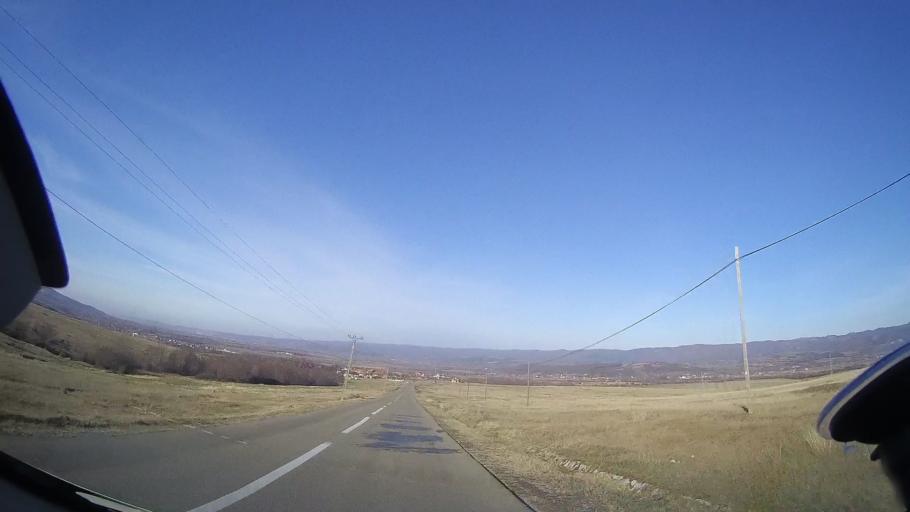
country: RO
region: Bihor
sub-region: Comuna Vadu Crisului
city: Vadu Crisului
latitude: 46.9785
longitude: 22.5333
